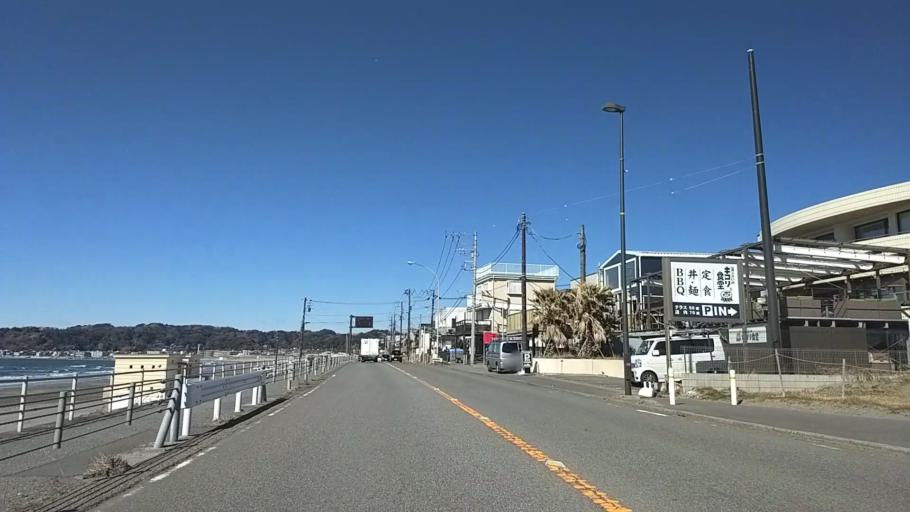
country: JP
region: Kanagawa
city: Kamakura
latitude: 35.3044
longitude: 139.5519
